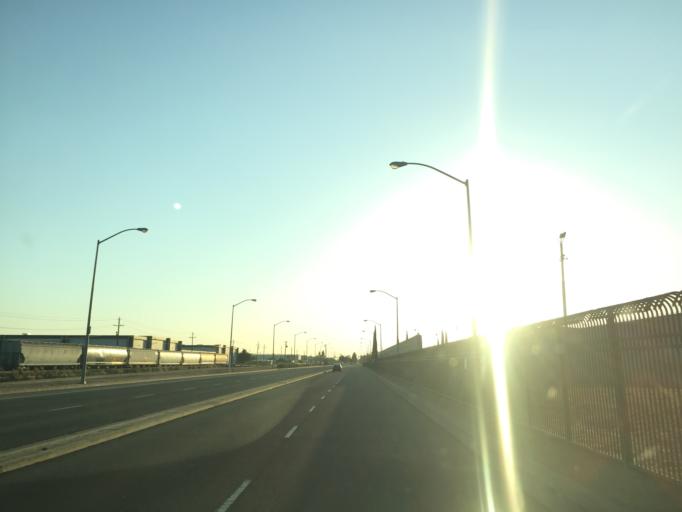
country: US
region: California
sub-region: Fresno County
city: Sunnyside
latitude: 36.7653
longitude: -119.7055
